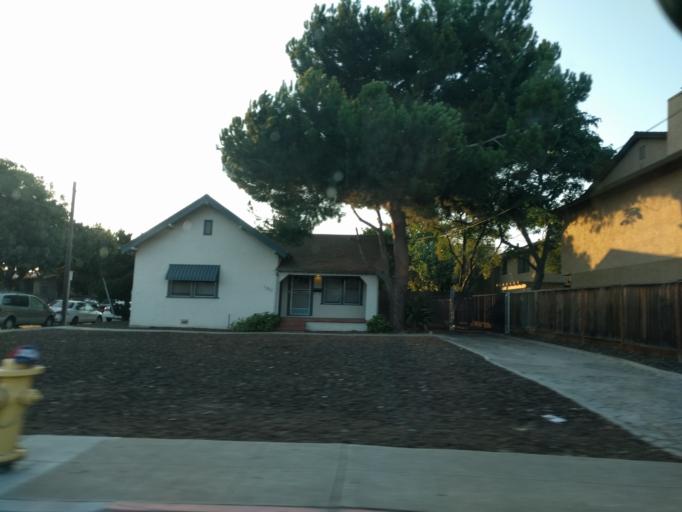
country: US
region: California
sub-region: Santa Clara County
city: San Jose
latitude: 37.3519
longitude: -121.8701
